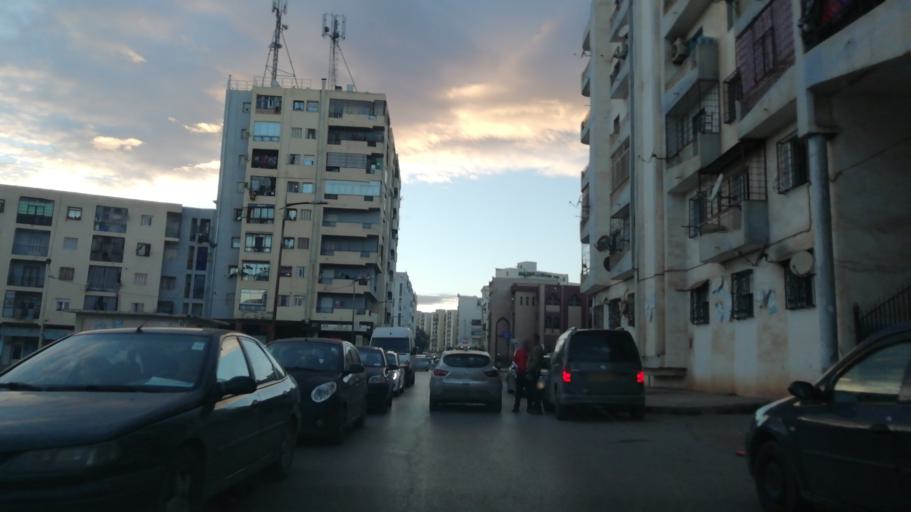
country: DZ
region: Oran
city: Bir el Djir
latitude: 35.6985
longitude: -0.5646
